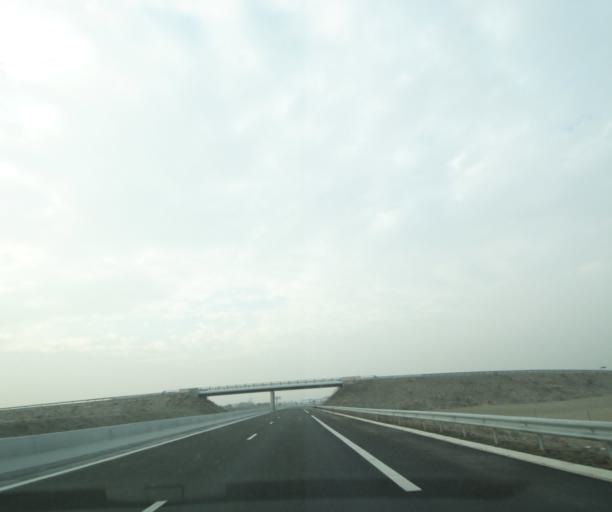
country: FR
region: Rhone-Alpes
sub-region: Departement du Rhone
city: Les Cheres
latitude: 45.9131
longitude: 4.7410
